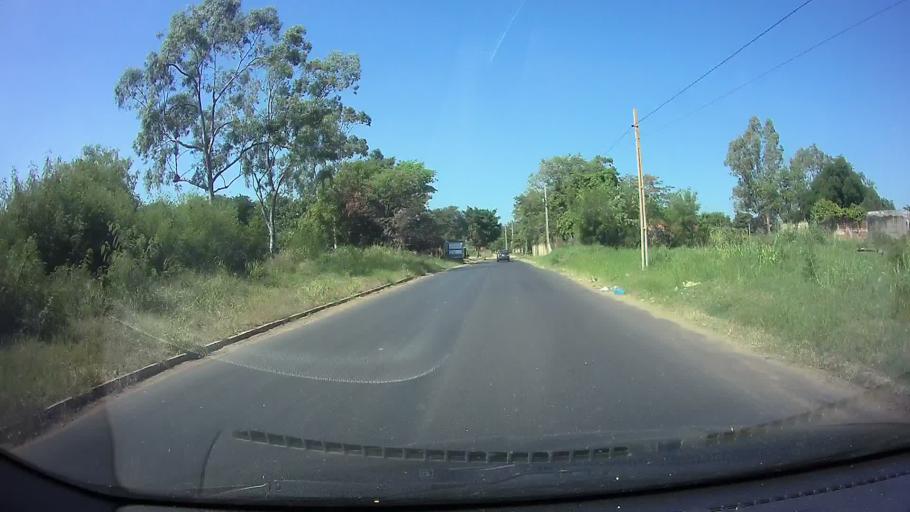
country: PY
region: Central
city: Fernando de la Mora
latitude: -25.2850
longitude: -57.5429
